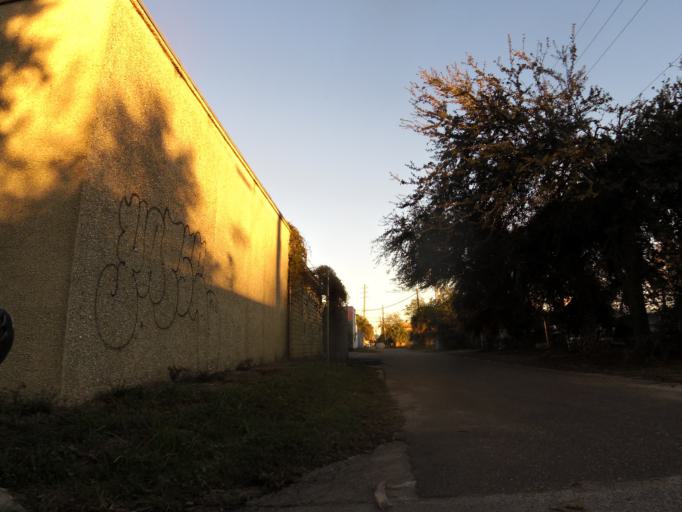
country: US
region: Florida
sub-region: Duval County
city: Jacksonville
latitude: 30.3201
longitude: -81.6980
